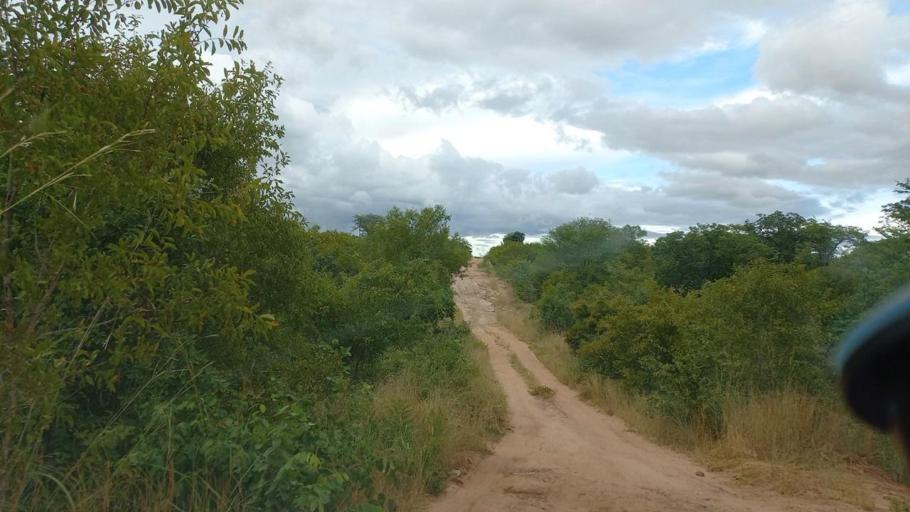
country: ZM
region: Lusaka
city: Luangwa
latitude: -15.5640
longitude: 30.3434
